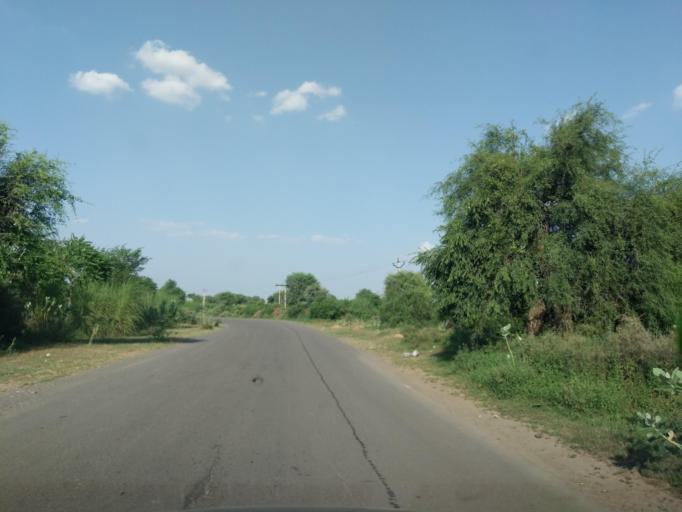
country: IN
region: Rajasthan
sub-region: Churu
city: Rajgarh
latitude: 28.4982
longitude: 75.3792
